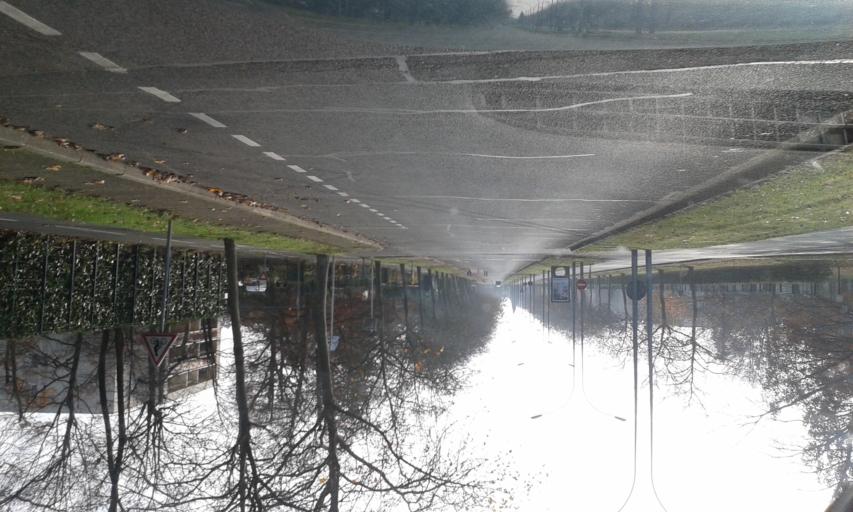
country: FR
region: Centre
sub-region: Departement du Loiret
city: Saint-Cyr-en-Val
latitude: 47.8286
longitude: 1.9361
